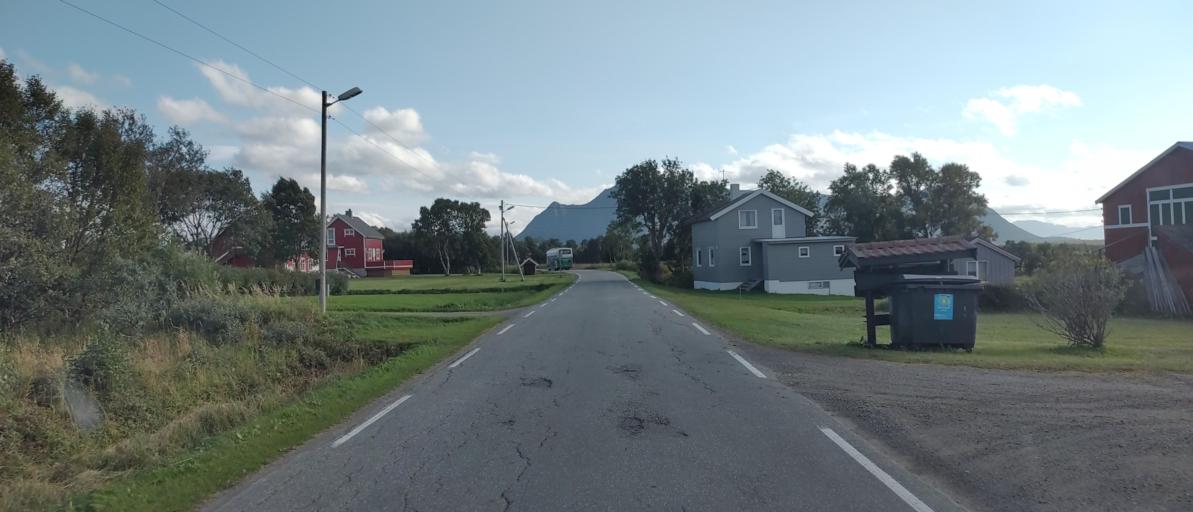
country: NO
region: Nordland
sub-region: Sortland
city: Sortland
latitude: 69.0413
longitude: 15.5157
